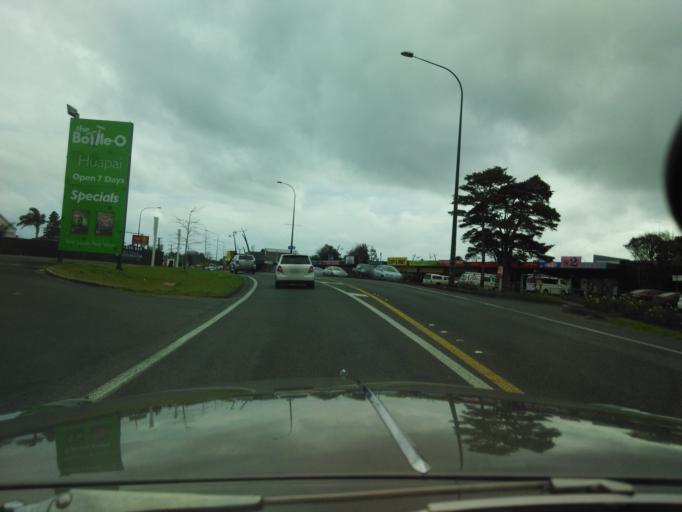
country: NZ
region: Auckland
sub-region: Auckland
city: Muriwai Beach
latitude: -36.7726
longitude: 174.5477
